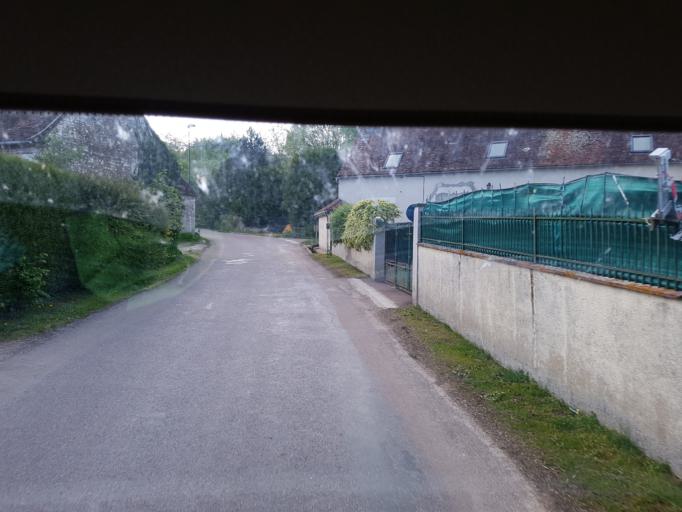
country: FR
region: Bourgogne
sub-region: Departement de l'Yonne
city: Neuvy-Sautour
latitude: 48.0547
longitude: 3.7694
